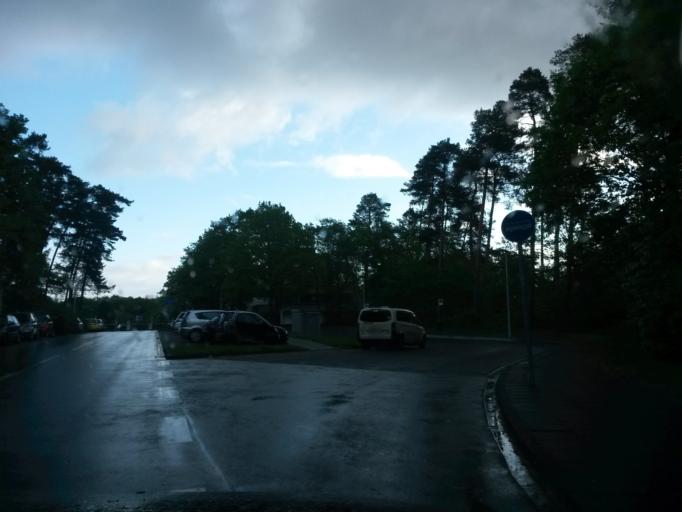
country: DE
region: North Rhine-Westphalia
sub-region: Regierungsbezirk Koln
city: Alfter
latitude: 50.7062
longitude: 7.0337
